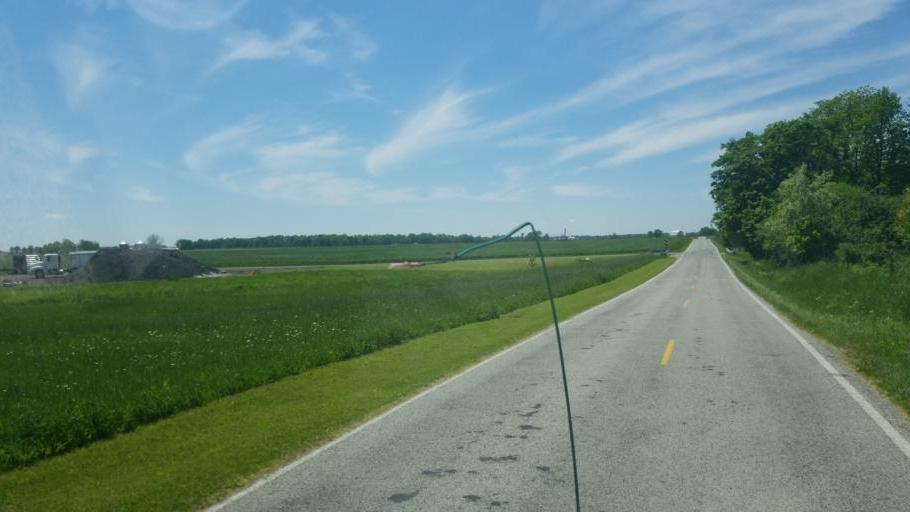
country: US
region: Ohio
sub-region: Huron County
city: Norwalk
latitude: 41.1892
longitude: -82.5586
